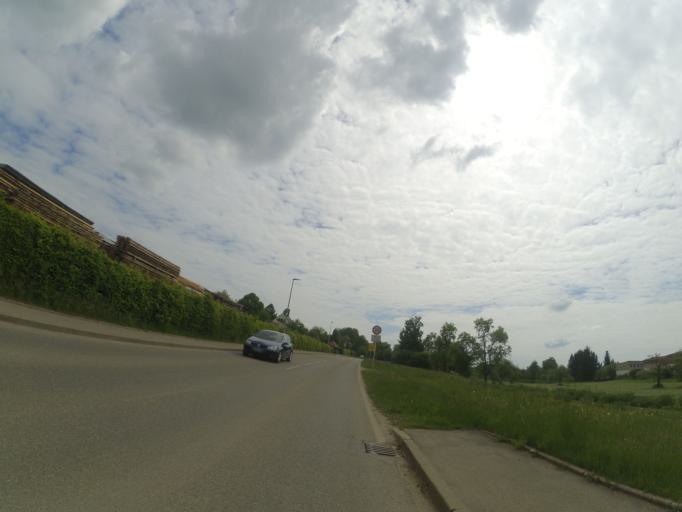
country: DE
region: Baden-Wuerttemberg
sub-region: Tuebingen Region
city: Berghulen
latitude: 48.4633
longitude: 9.7672
